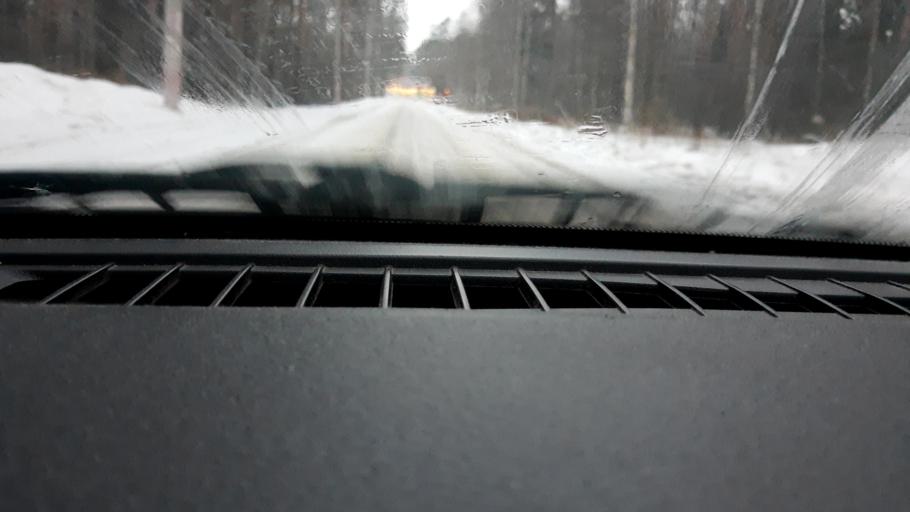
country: RU
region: Nizjnij Novgorod
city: Afonino
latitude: 56.1728
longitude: 44.0848
